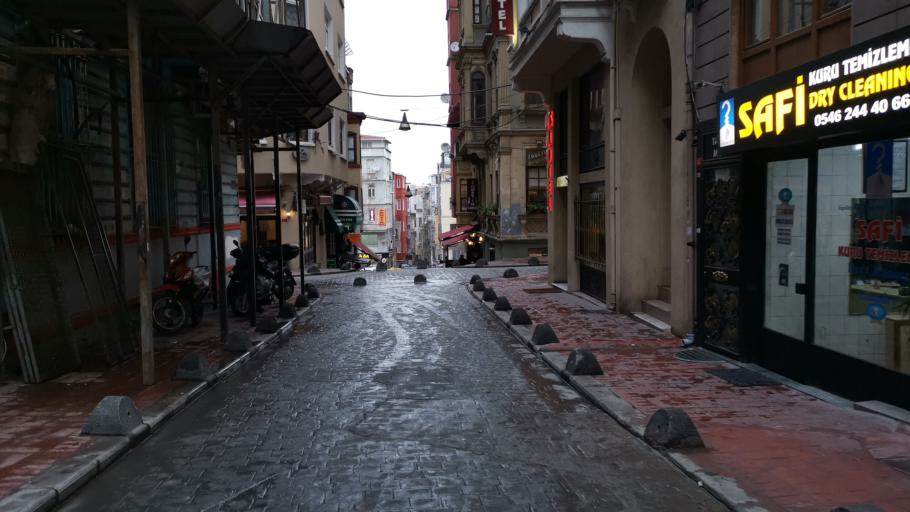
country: TR
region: Istanbul
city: Eminoenue
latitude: 41.0362
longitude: 28.9822
